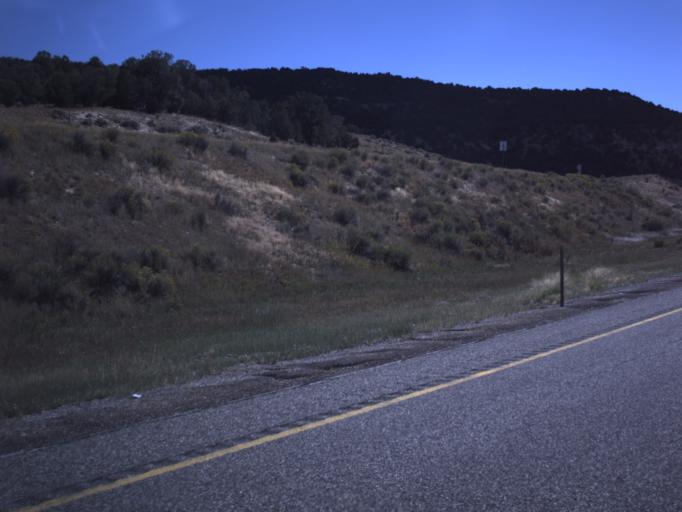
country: US
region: Utah
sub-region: Sevier County
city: Salina
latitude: 38.8531
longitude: -111.5486
